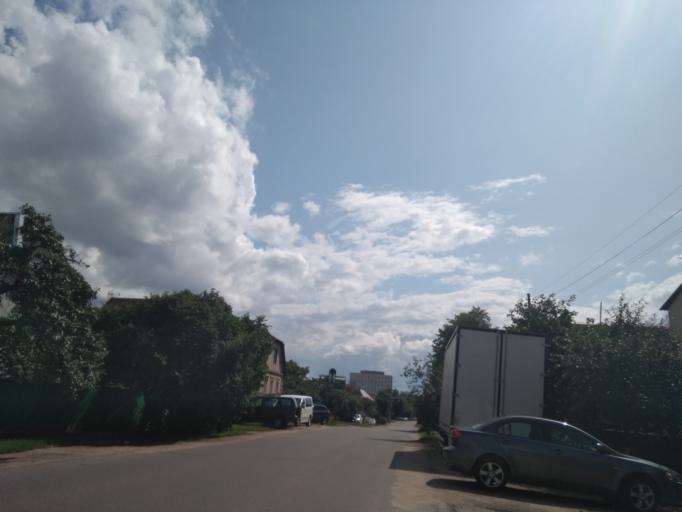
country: BY
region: Minsk
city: Minsk
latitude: 53.9372
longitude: 27.5556
